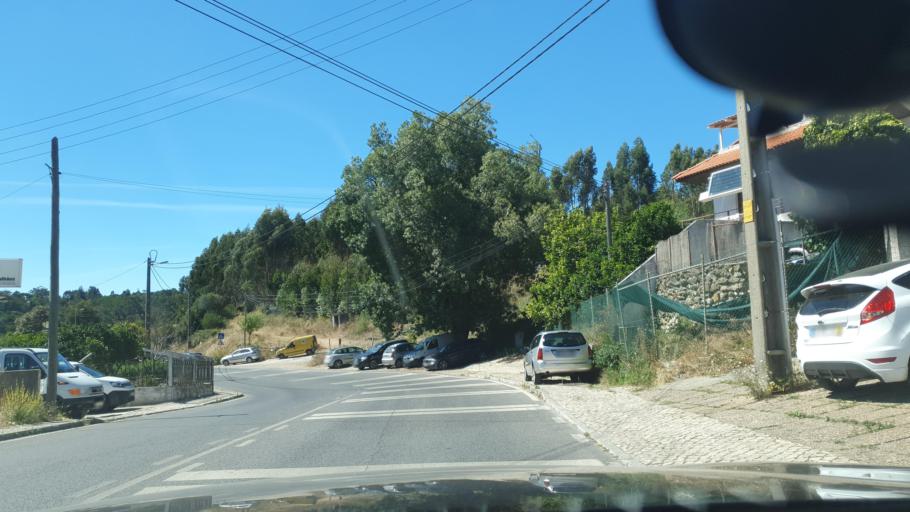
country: PT
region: Lisbon
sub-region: Sintra
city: Belas
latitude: 38.7824
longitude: -9.2575
